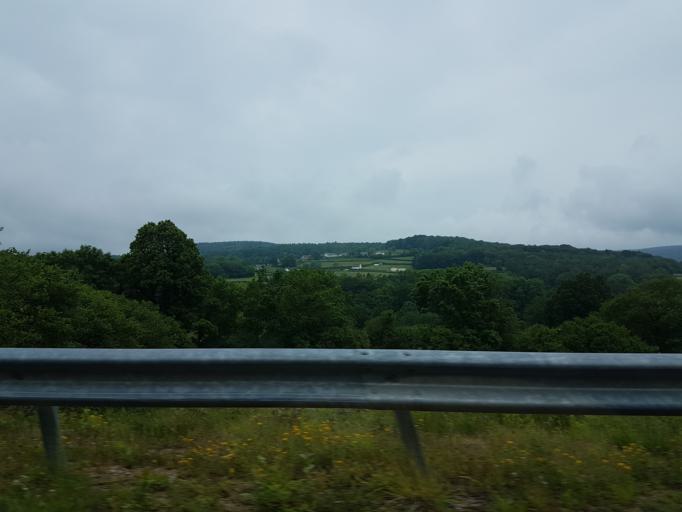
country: FR
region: Bourgogne
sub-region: Departement de la Nievre
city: Chateau-Chinon(Ville)
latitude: 47.0504
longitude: 3.9803
